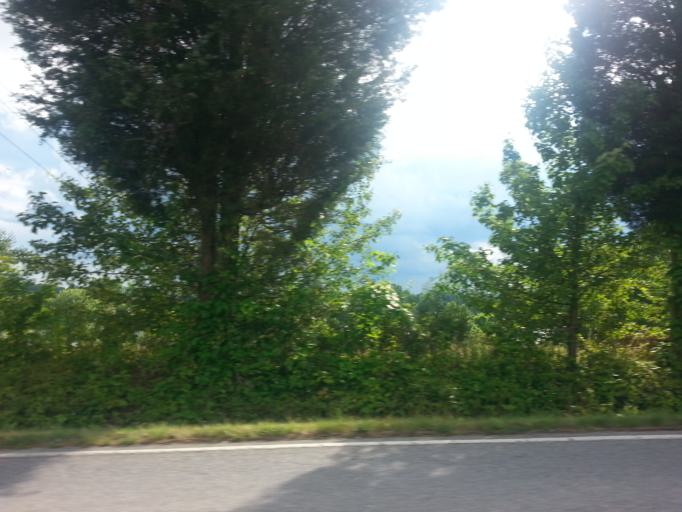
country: US
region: Tennessee
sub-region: Blount County
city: Louisville
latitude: 35.8124
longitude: -84.0276
